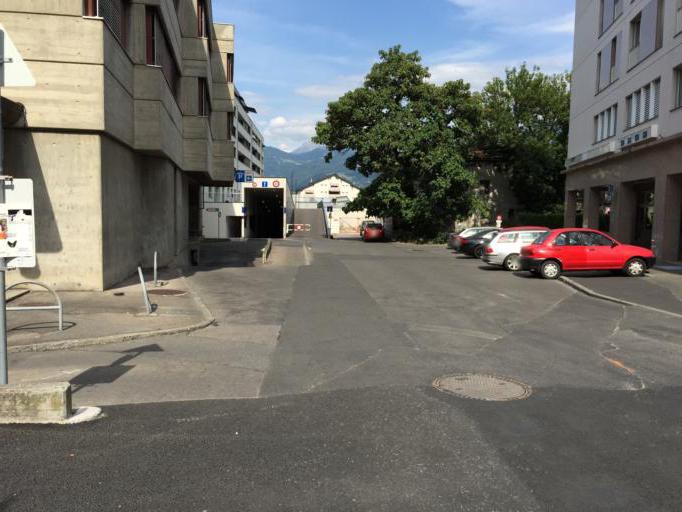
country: CH
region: Valais
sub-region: Monthey District
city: Monthey
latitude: 46.2528
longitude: 6.9504
